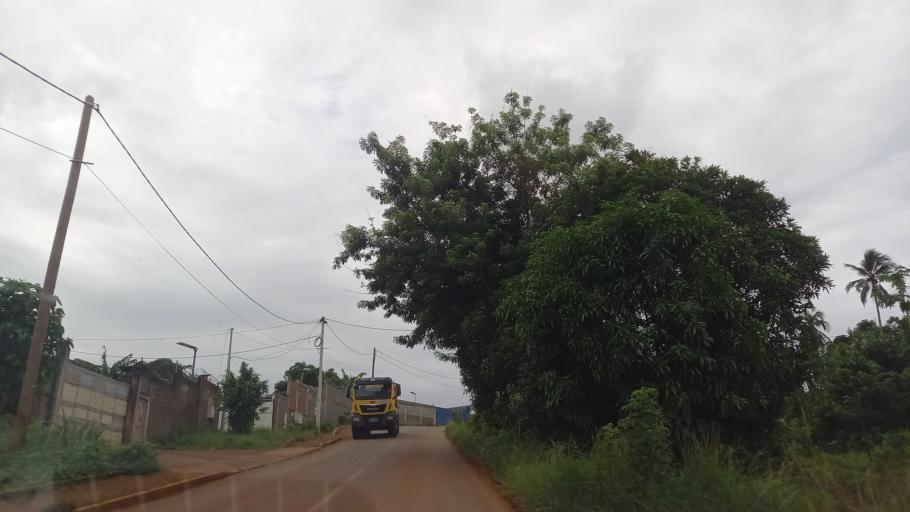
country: YT
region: Chiconi
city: Chiconi
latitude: -12.8279
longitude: 45.1284
